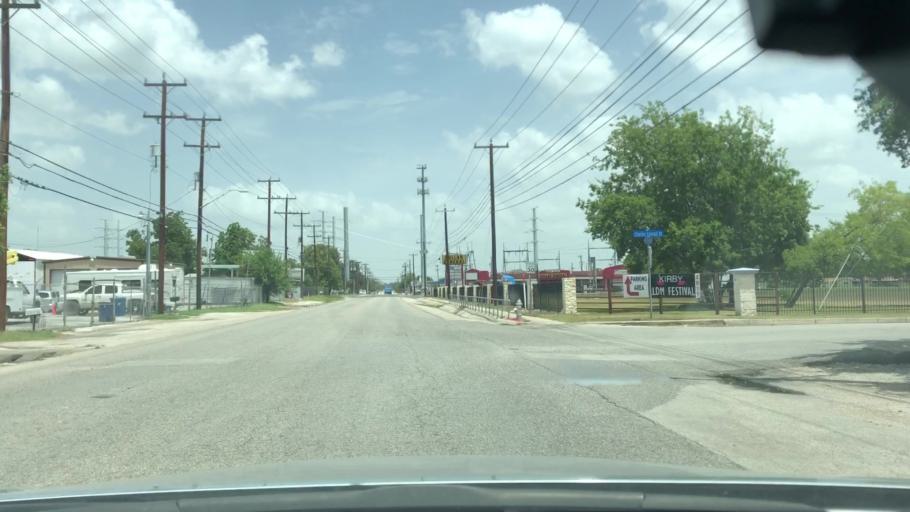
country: US
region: Texas
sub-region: Bexar County
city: Kirby
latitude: 29.4646
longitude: -98.3955
